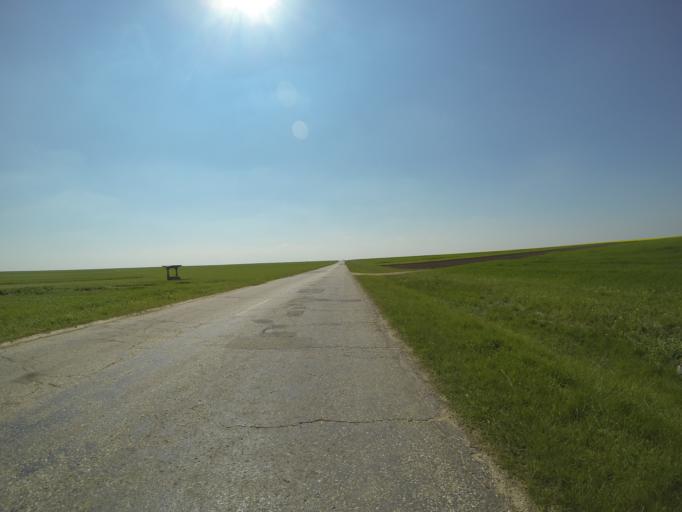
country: RO
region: Dolj
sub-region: Comuna Caraula
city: Caraula
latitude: 44.1834
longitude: 23.2247
